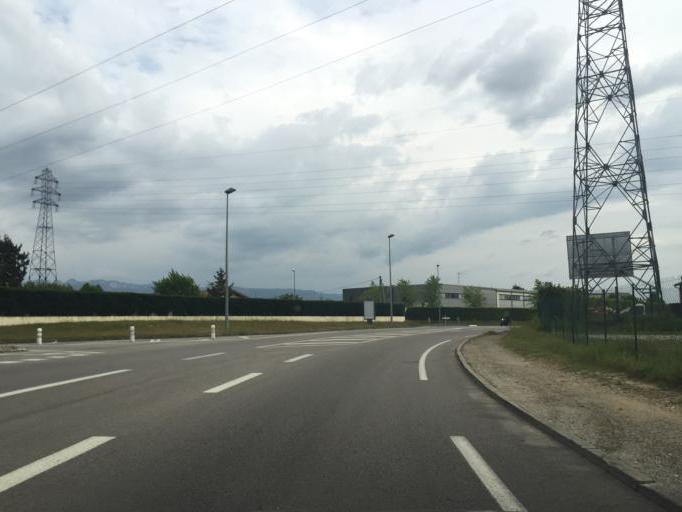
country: FR
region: Rhone-Alpes
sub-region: Departement de la Drome
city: Romans-sur-Isere
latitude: 45.0227
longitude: 5.0415
